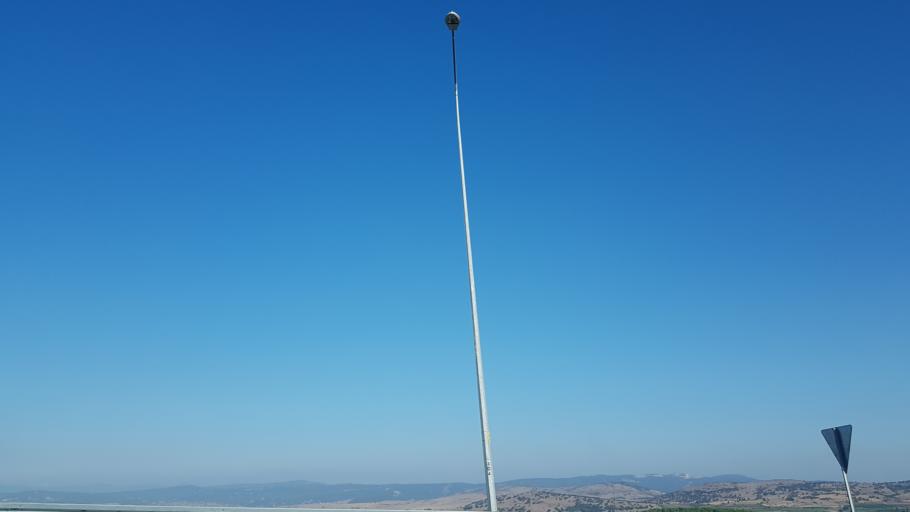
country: TR
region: Balikesir
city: Ertugrul
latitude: 39.6348
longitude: 27.7111
